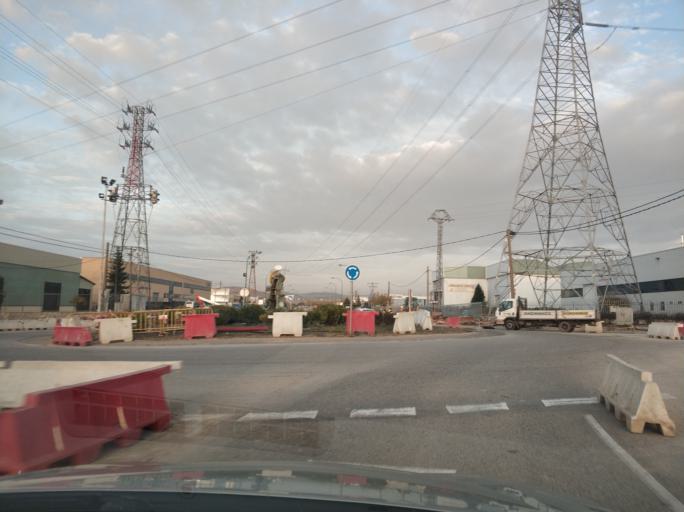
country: ES
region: Castille and Leon
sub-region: Provincia de Burgos
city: Sotragero
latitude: 42.3712
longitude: -3.7307
